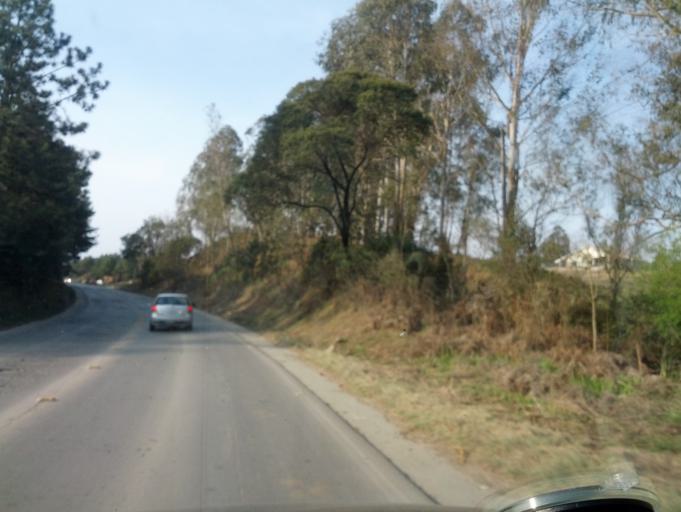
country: BR
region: Santa Catarina
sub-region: Otacilio Costa
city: Otacilio Costa
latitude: -27.5726
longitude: -50.1532
